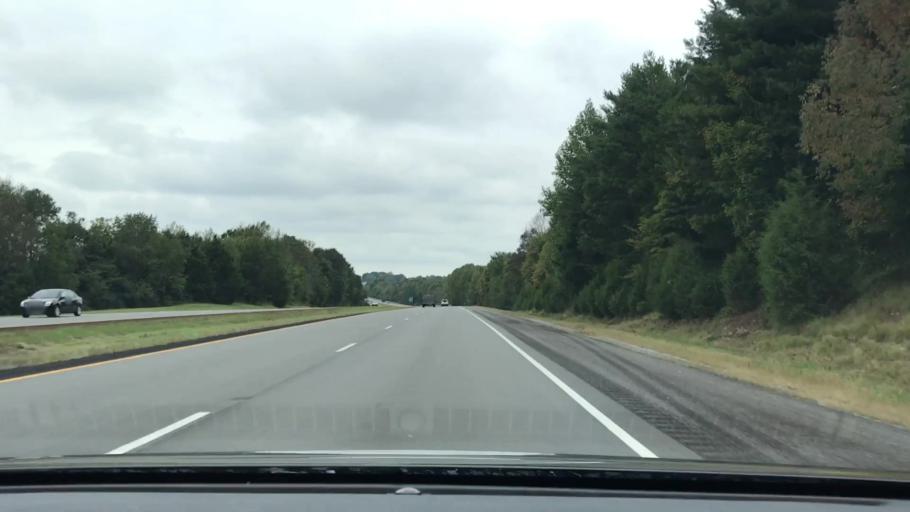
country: US
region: Kentucky
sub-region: Barren County
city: Glasgow
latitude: 36.9974
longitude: -85.8431
